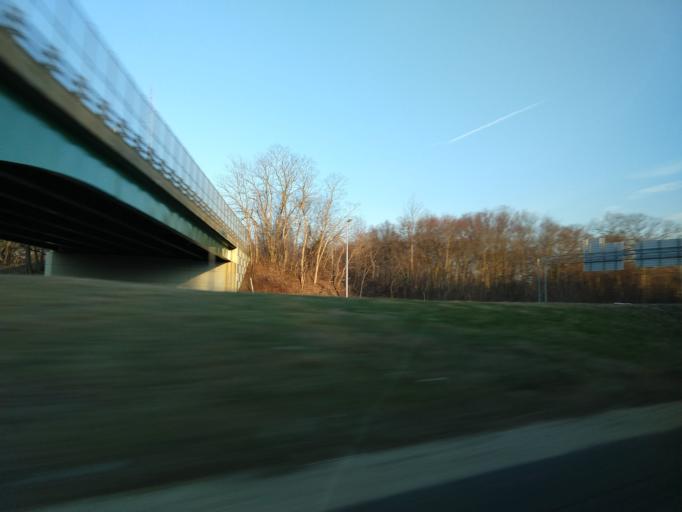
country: US
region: Massachusetts
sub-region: Essex County
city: South Peabody
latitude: 42.5328
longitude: -70.9817
